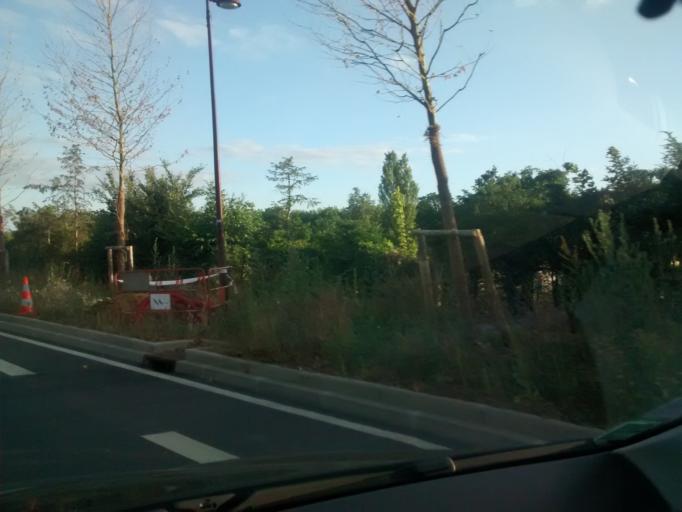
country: FR
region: Ile-de-France
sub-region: Departement des Yvelines
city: Le Chesnay
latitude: 48.8243
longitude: 2.1143
